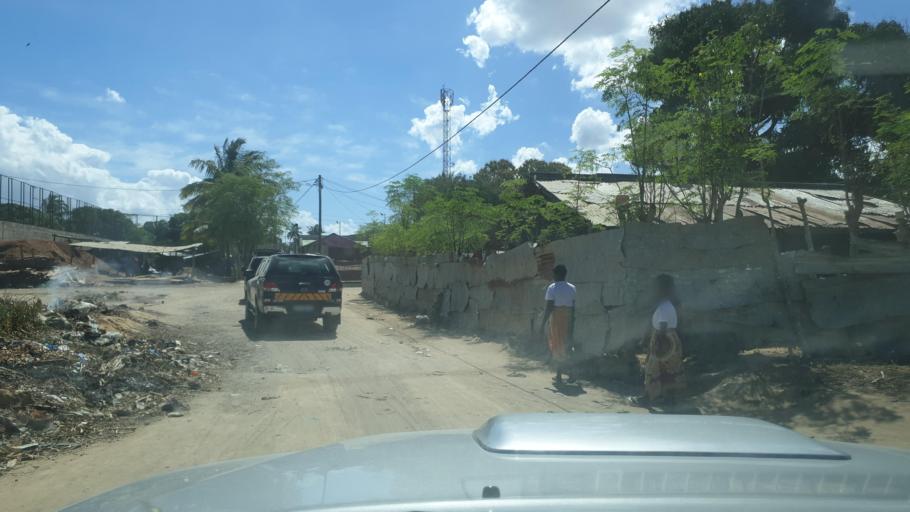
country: MZ
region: Nampula
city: Nacala
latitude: -14.5711
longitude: 40.6865
